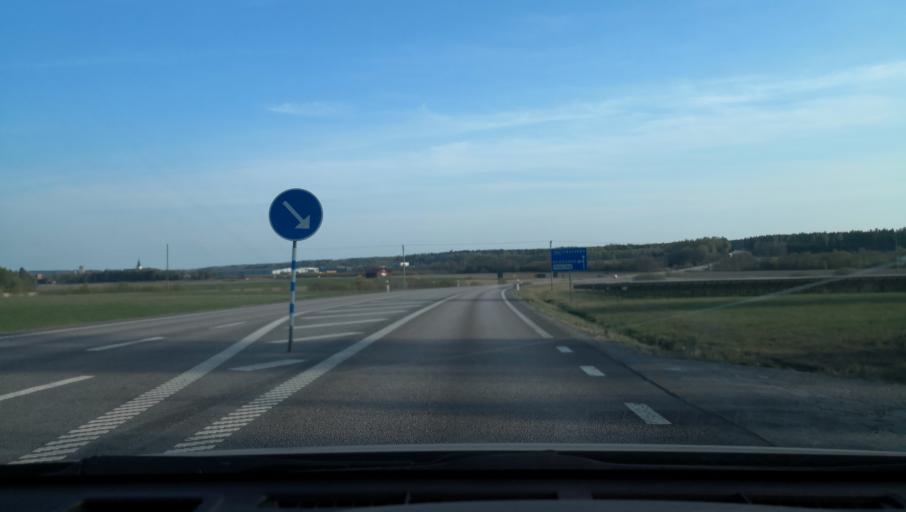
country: SE
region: Uppsala
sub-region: Heby Kommun
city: Heby
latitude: 59.9572
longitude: 16.8389
